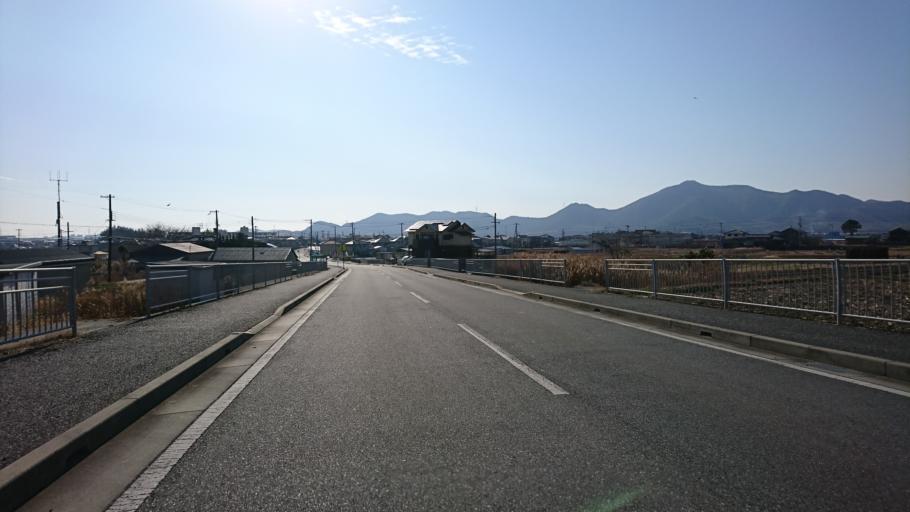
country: JP
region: Hyogo
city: Kakogawacho-honmachi
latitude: 34.8236
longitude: 134.8252
